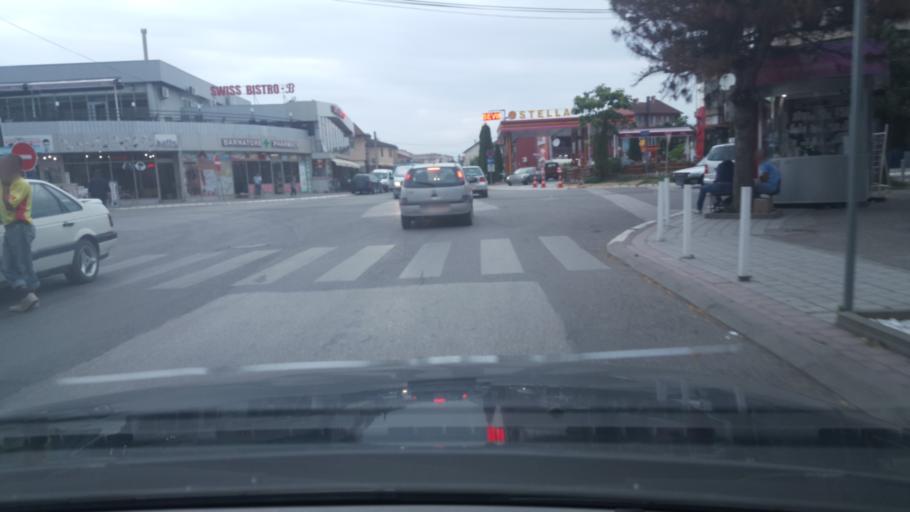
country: XK
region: Gjakova
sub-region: Komuna e Gjakoves
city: Gjakove
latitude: 42.3880
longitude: 20.4323
